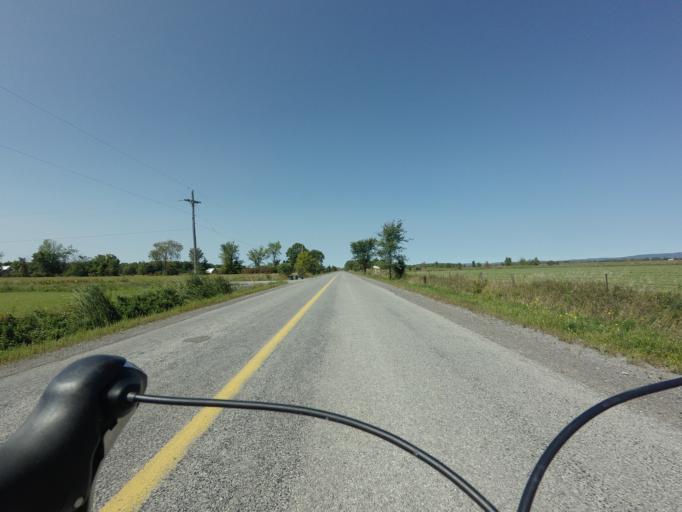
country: CA
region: Ontario
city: Bells Corners
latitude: 45.4410
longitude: -76.0715
